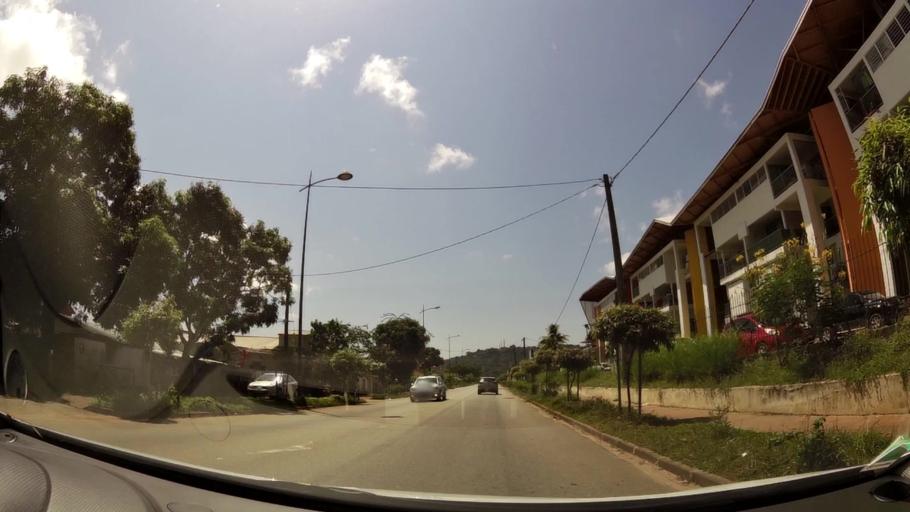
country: GF
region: Guyane
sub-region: Guyane
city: Cayenne
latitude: 4.9205
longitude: -52.3211
